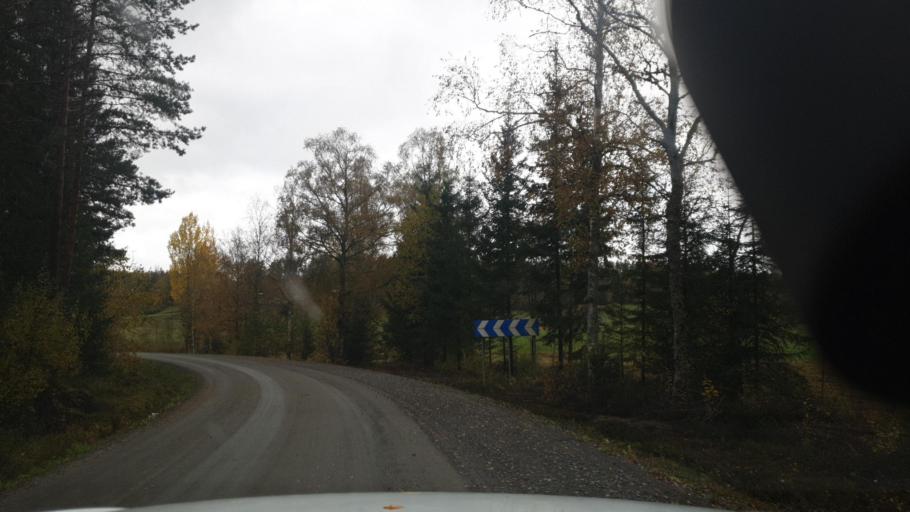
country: SE
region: Vaermland
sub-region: Karlstads Kommun
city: Edsvalla
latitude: 59.4513
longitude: 13.1286
